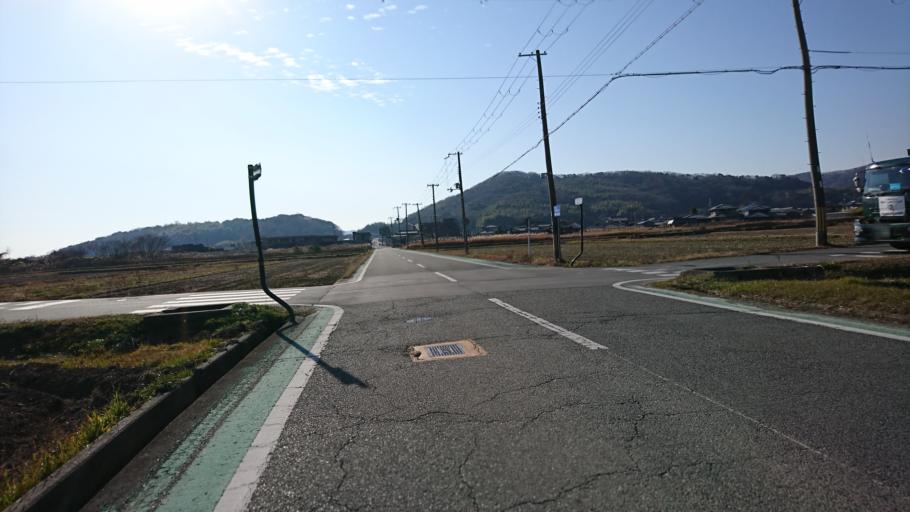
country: JP
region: Hyogo
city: Kakogawacho-honmachi
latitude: 34.8310
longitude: 134.8348
